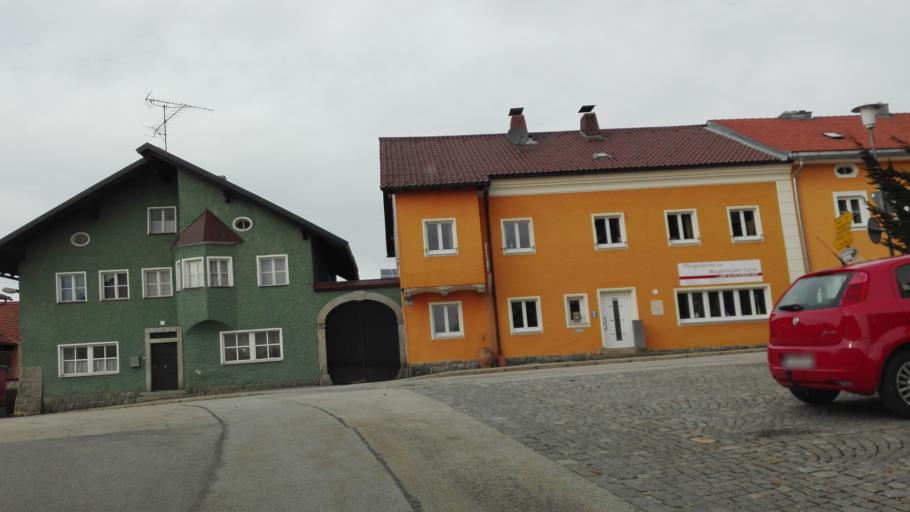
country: DE
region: Bavaria
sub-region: Lower Bavaria
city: Wegscheid
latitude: 48.6012
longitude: 13.7858
